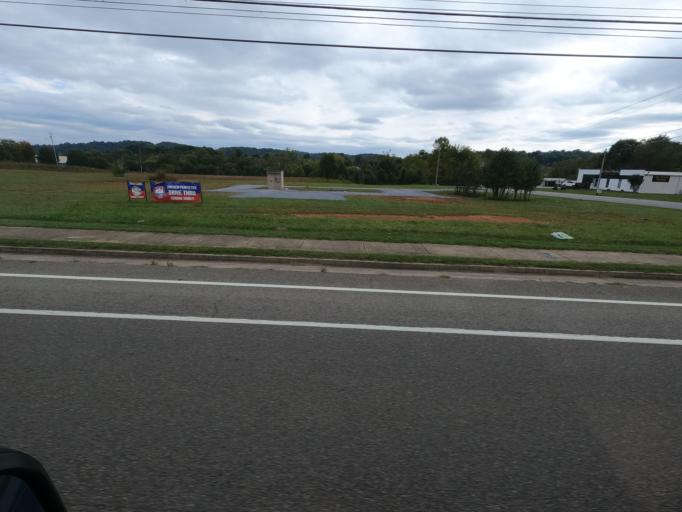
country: US
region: Tennessee
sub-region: Washington County
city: Oak Grove
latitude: 36.3846
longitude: -82.4175
